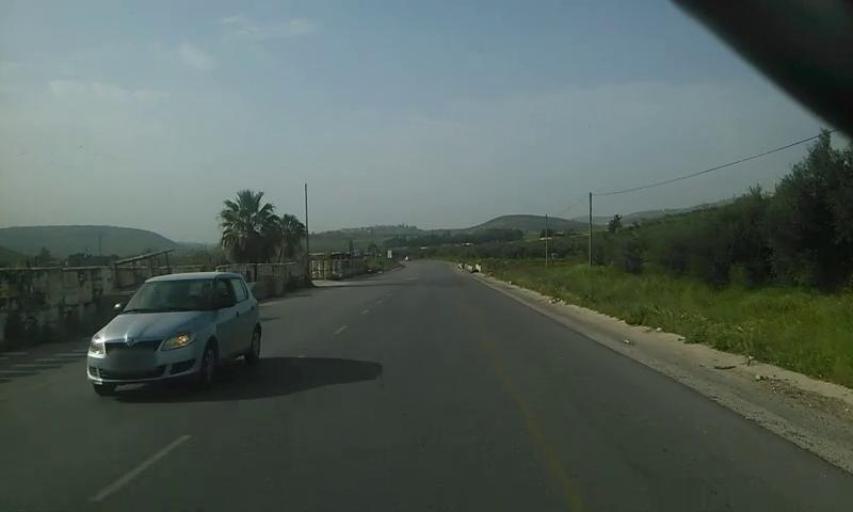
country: PS
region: West Bank
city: Dayr Sharaf
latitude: 32.2621
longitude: 35.1735
